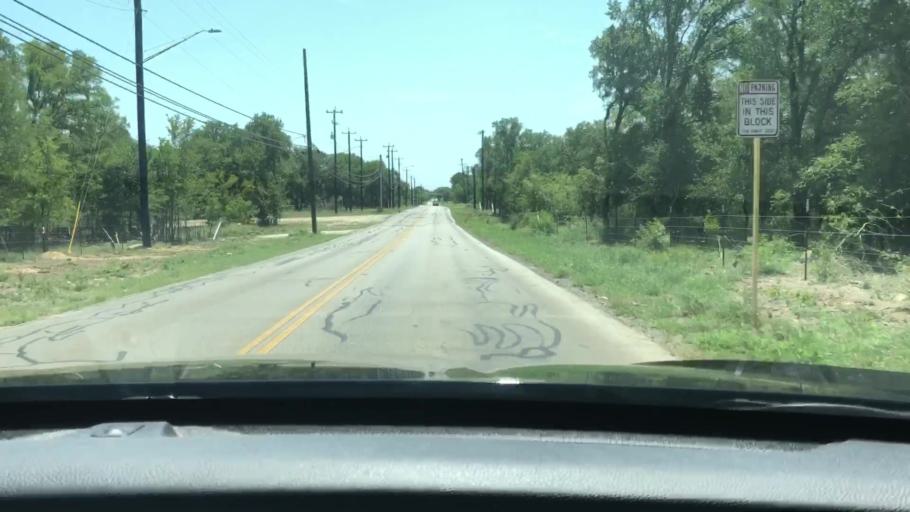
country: US
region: Texas
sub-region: Bexar County
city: Helotes
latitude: 29.5567
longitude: -98.6558
